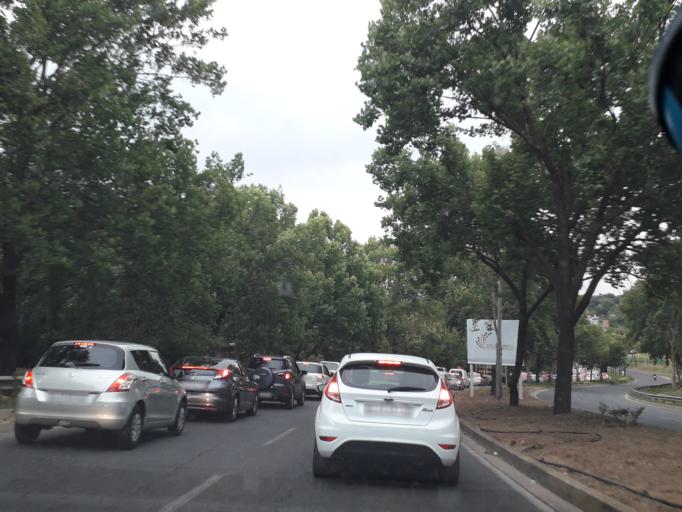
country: ZA
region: Gauteng
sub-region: City of Johannesburg Metropolitan Municipality
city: Johannesburg
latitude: -26.1084
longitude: 28.0478
